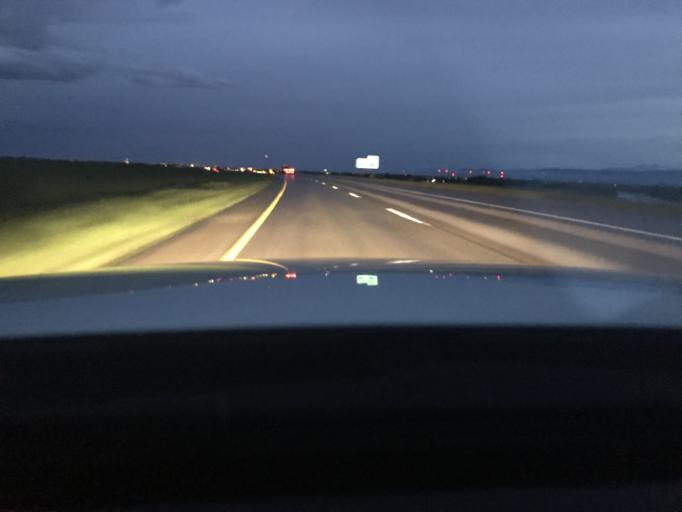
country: US
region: Colorado
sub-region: Larimer County
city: Wellington
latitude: 40.7617
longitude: -104.9921
